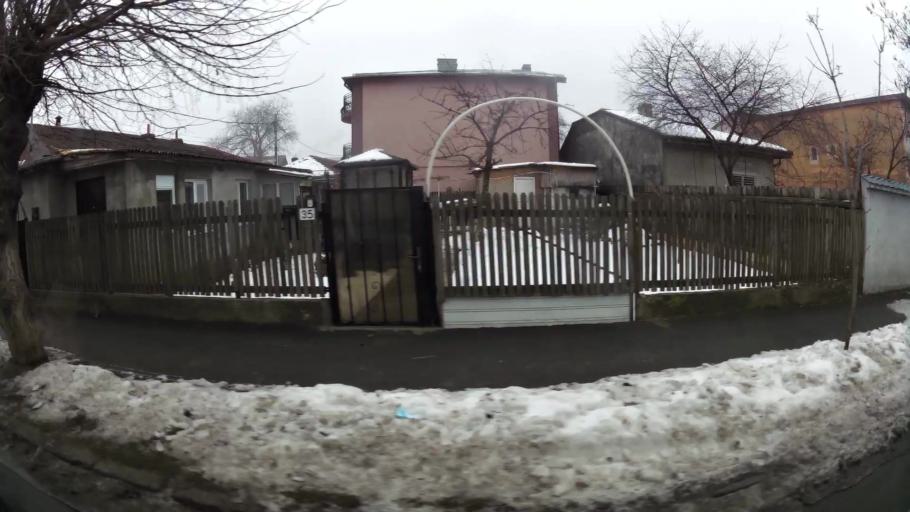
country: RO
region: Ilfov
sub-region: Comuna Chiajna
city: Rosu
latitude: 44.4447
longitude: 26.0127
